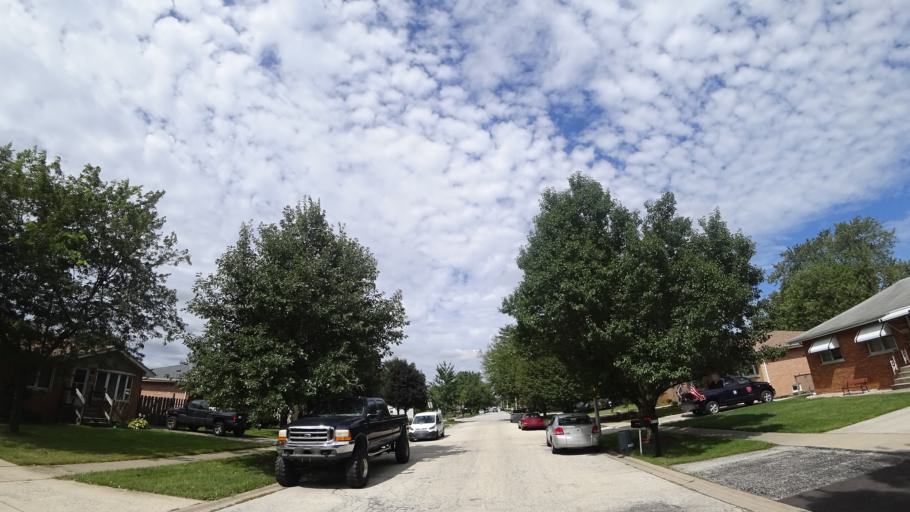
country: US
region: Illinois
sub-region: Cook County
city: Chicago Ridge
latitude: 41.7151
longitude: -87.7883
